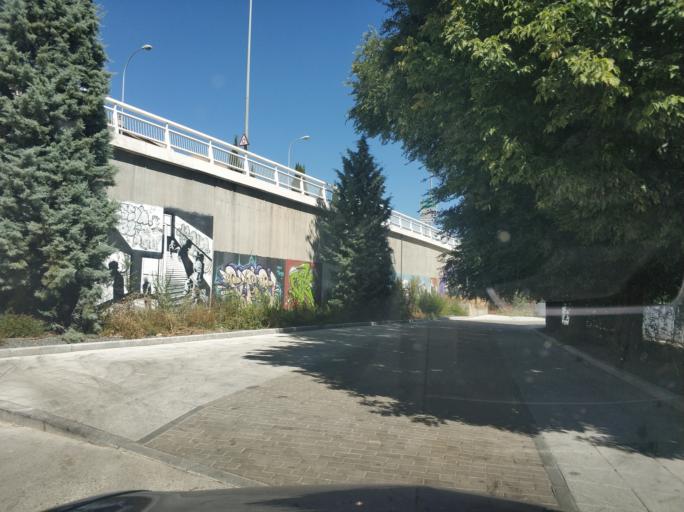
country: ES
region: Castille and Leon
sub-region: Provincia de Salamanca
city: Salamanca
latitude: 40.9581
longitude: -5.6622
